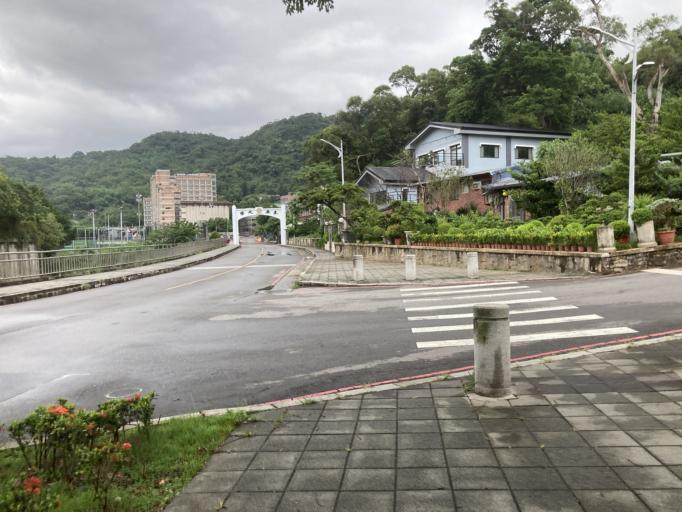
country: TW
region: Taipei
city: Taipei
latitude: 25.0962
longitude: 121.5432
